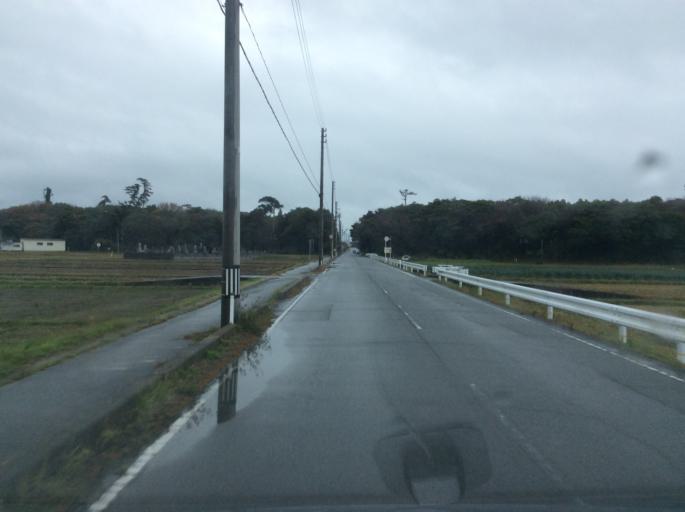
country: JP
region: Fukushima
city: Iwaki
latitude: 37.0671
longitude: 140.9667
